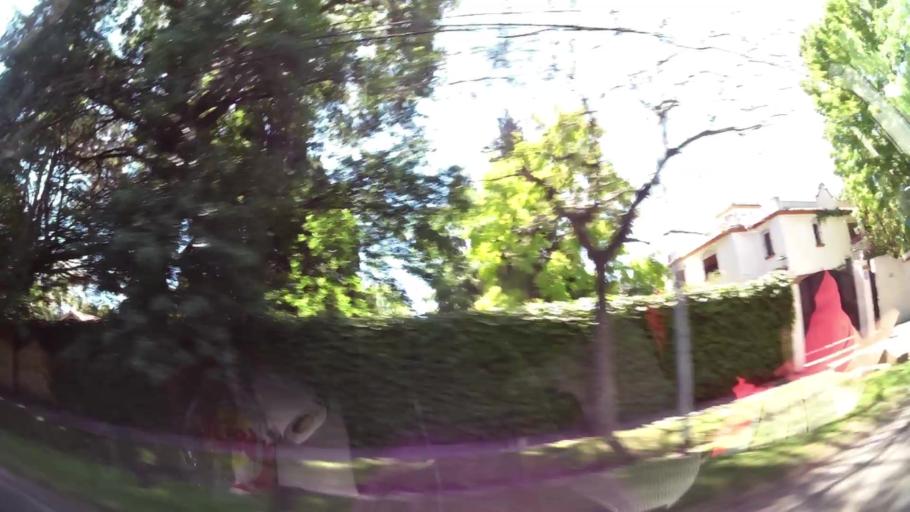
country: AR
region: Buenos Aires
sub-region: Partido de Tigre
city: Tigre
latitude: -34.4911
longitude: -58.6314
